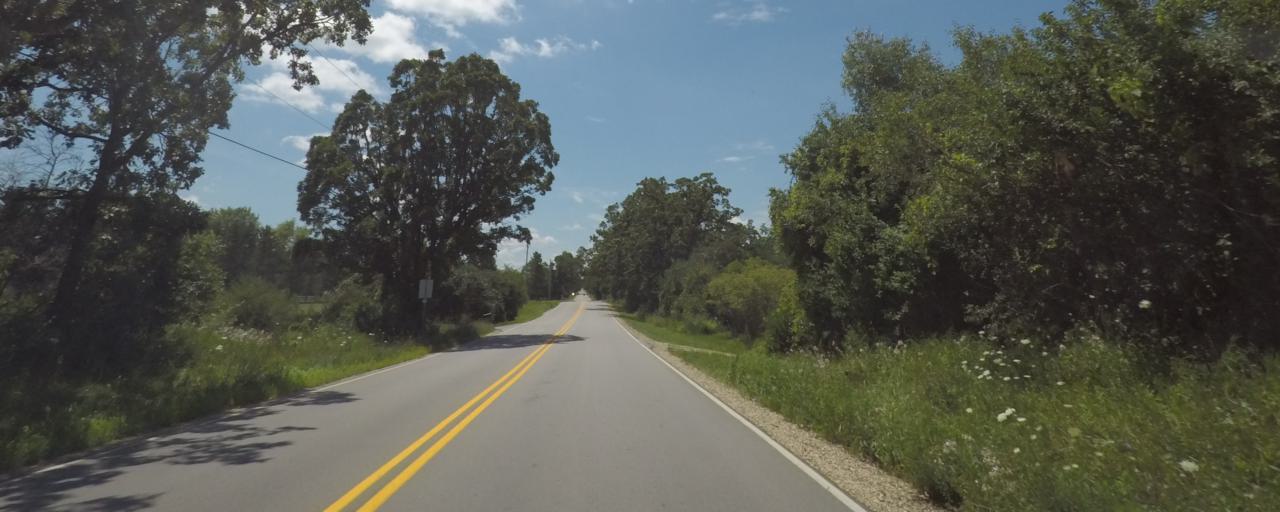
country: US
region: Wisconsin
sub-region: Waukesha County
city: Dousman
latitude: 42.9703
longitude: -88.4574
